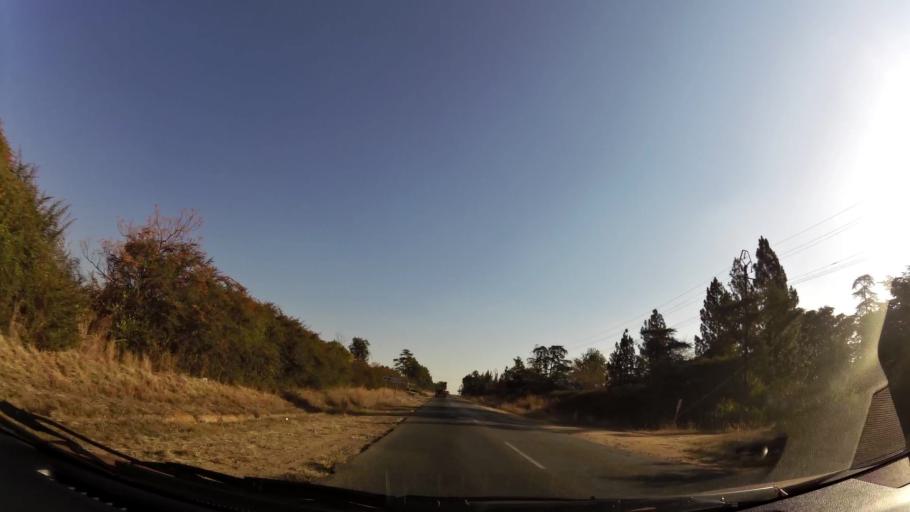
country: ZA
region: Gauteng
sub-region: West Rand District Municipality
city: Muldersdriseloop
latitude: -26.0166
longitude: 27.8854
